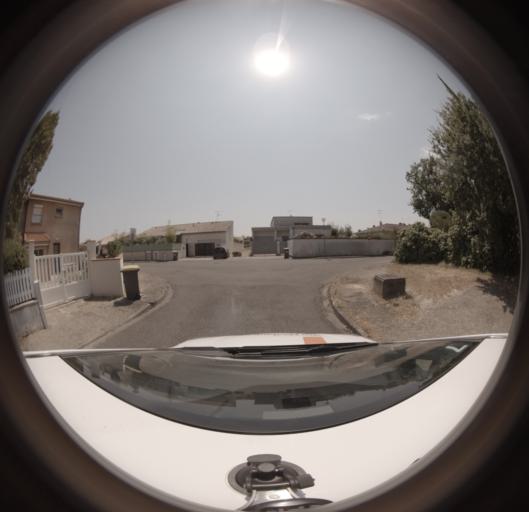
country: FR
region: Midi-Pyrenees
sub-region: Departement du Tarn-et-Garonne
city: Montauban
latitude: 44.0173
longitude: 1.3790
